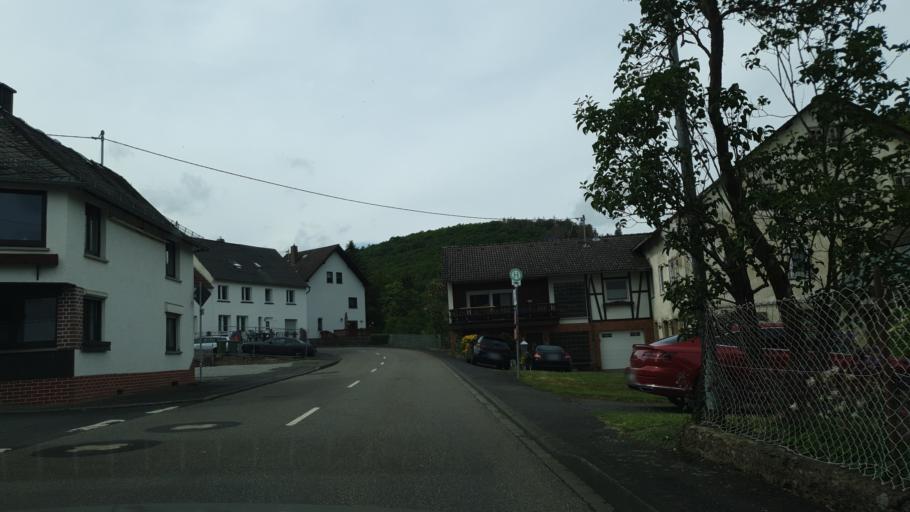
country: DE
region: Rheinland-Pfalz
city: Stahlhofen
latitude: 50.3961
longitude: 7.8807
